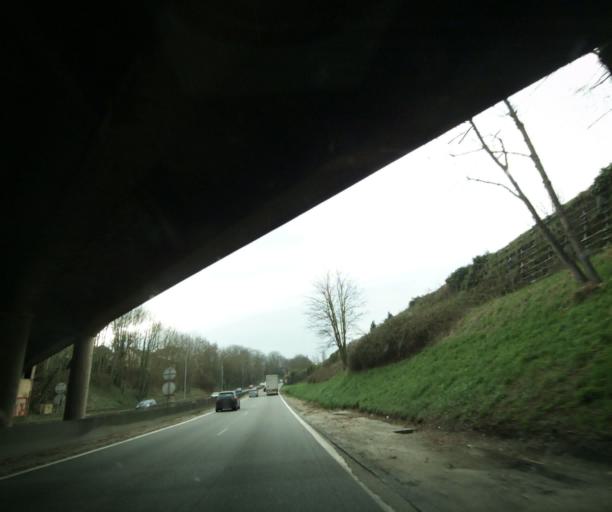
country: FR
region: Ile-de-France
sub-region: Departement des Yvelines
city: Le Pecq
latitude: 48.8866
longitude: 2.0955
